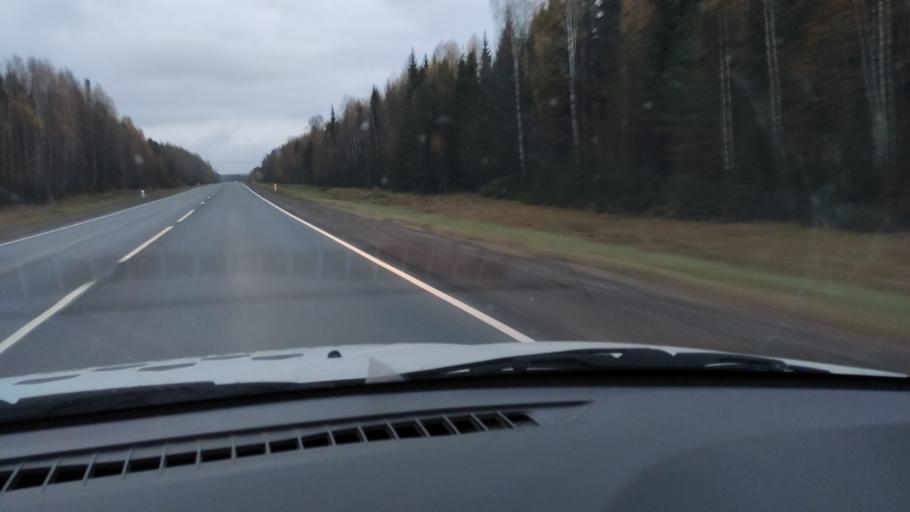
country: RU
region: Kirov
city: Kostino
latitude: 58.8596
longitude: 53.1096
